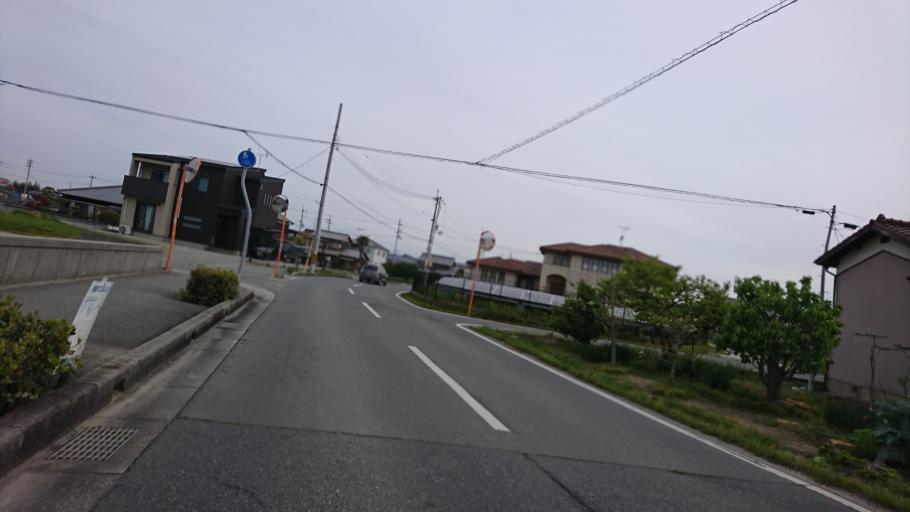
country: JP
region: Hyogo
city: Kakogawacho-honmachi
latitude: 34.7653
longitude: 134.9082
